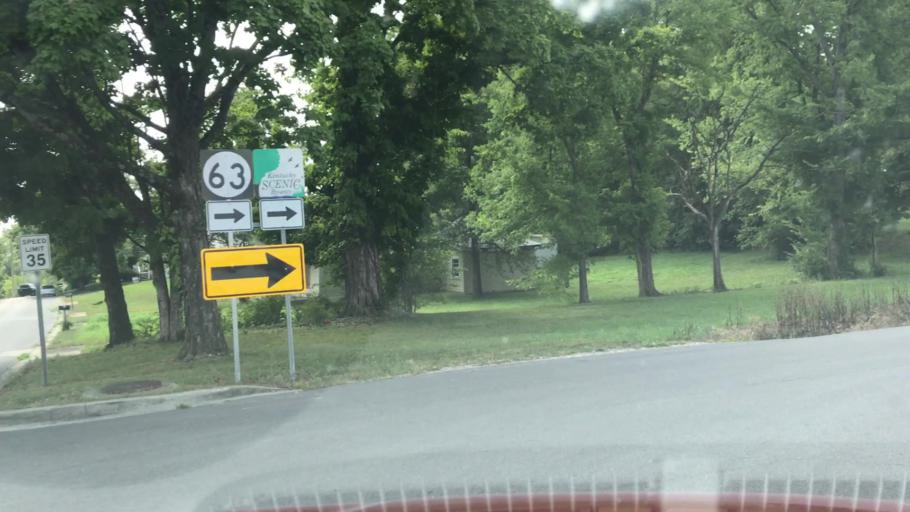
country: US
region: Kentucky
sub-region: Barren County
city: Glasgow
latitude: 36.9916
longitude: -85.9093
